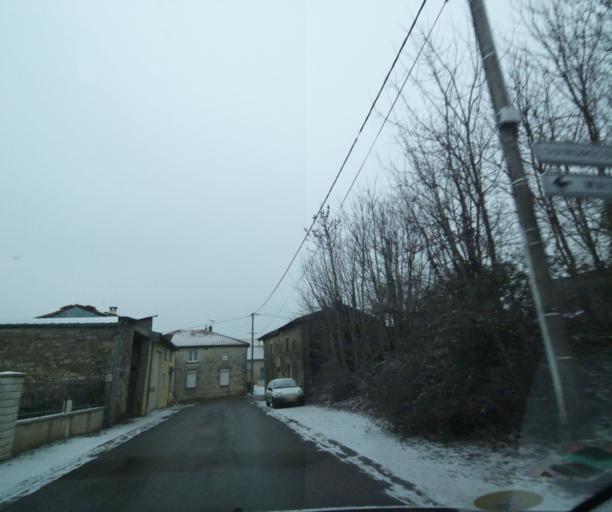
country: FR
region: Champagne-Ardenne
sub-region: Departement de la Haute-Marne
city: Wassy
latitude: 48.4749
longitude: 5.0353
